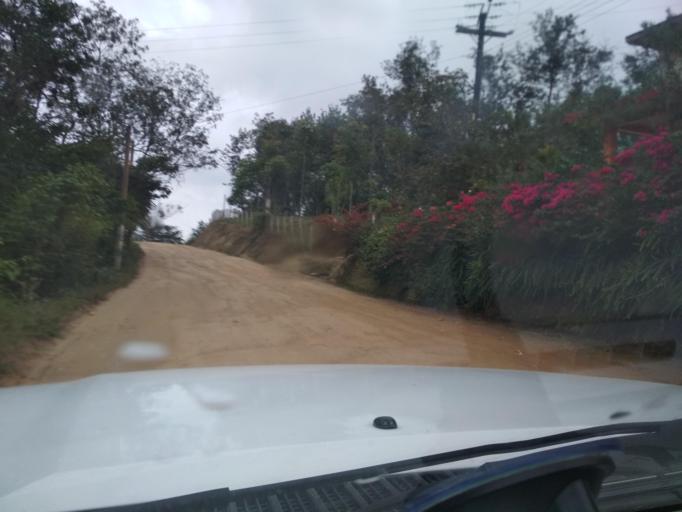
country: MX
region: Veracruz
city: El Castillo
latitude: 19.5430
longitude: -96.8311
